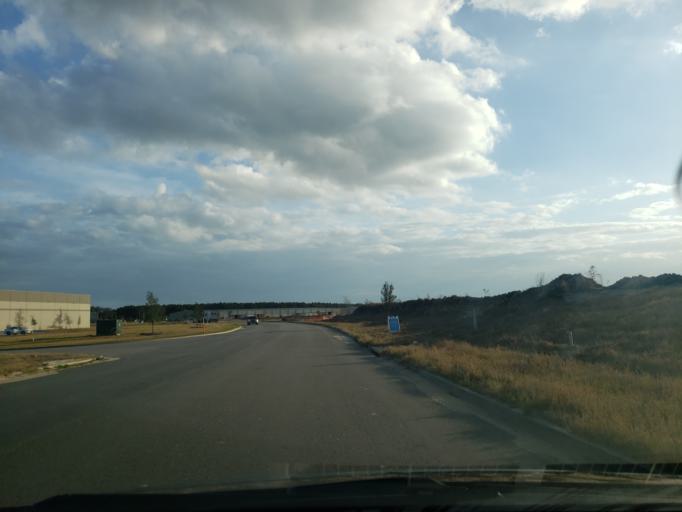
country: US
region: Georgia
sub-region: Chatham County
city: Bloomingdale
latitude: 32.1663
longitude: -81.2702
